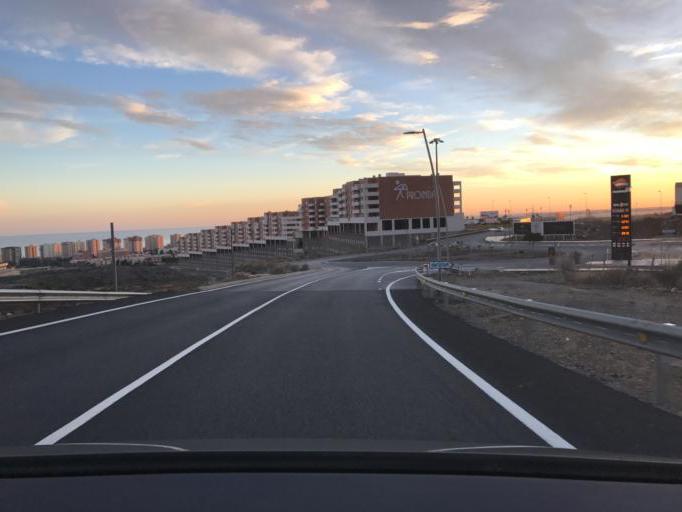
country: ES
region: Andalusia
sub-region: Provincia de Almeria
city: Aguadulce
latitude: 36.8234
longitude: -2.5818
